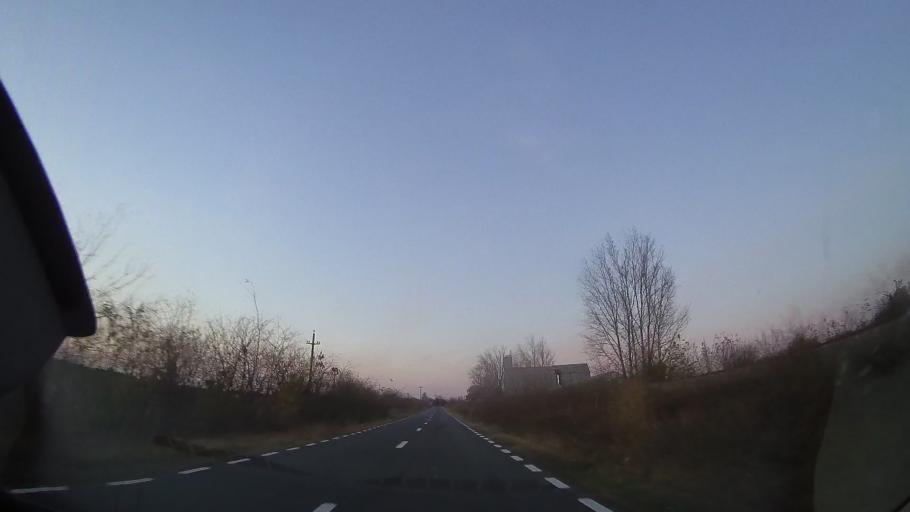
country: RO
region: Constanta
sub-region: Comuna Cobadin
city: Cobadin
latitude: 44.0490
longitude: 28.2501
